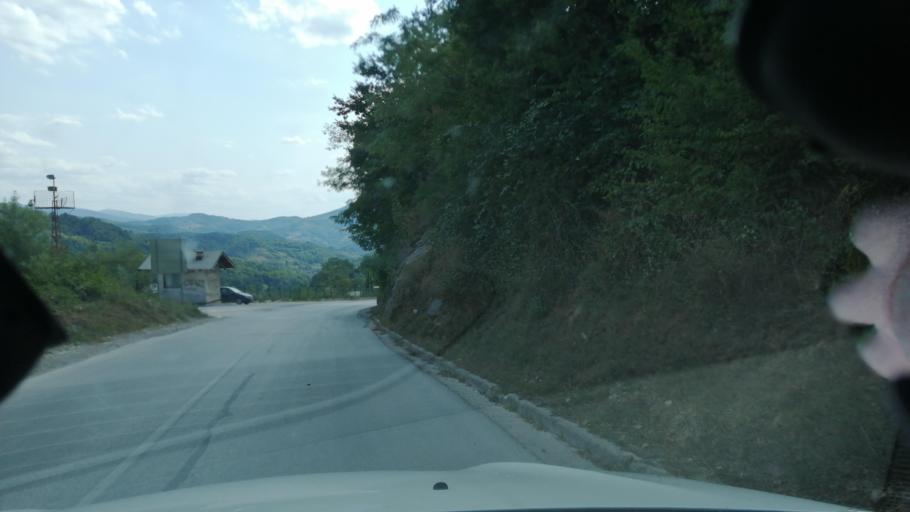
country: RS
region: Central Serbia
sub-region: Moravicki Okrug
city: Ivanjica
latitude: 43.6268
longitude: 20.2403
